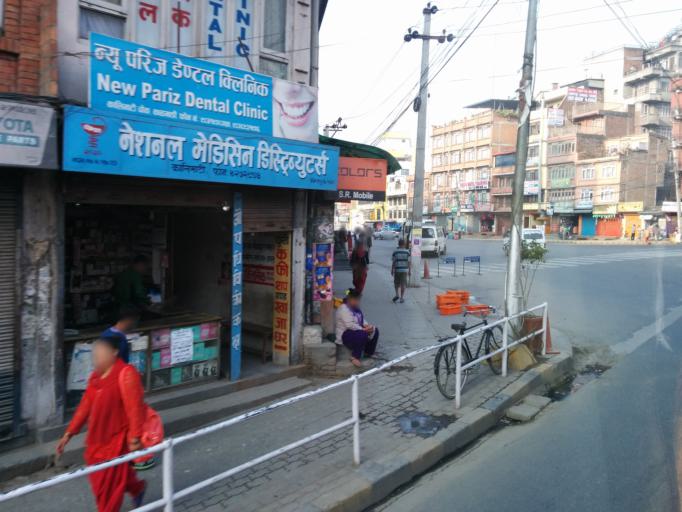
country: NP
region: Central Region
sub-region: Bagmati Zone
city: Kathmandu
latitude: 27.6984
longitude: 85.2998
